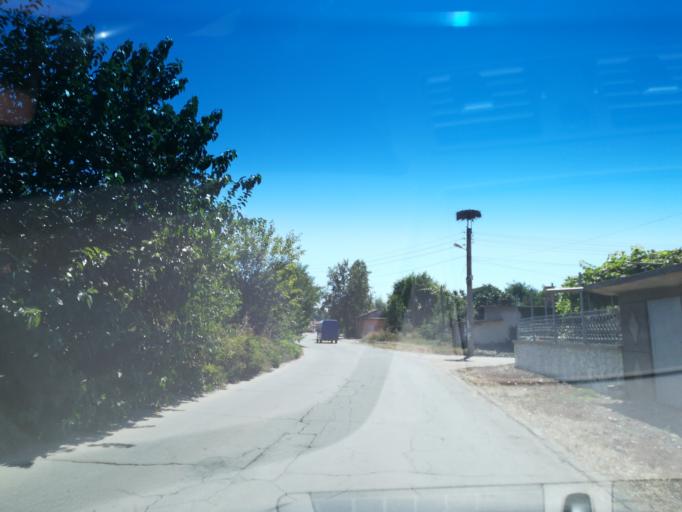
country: BG
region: Pazardzhik
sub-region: Obshtina Pazardzhik
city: Pazardzhik
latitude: 42.2757
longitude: 24.3964
